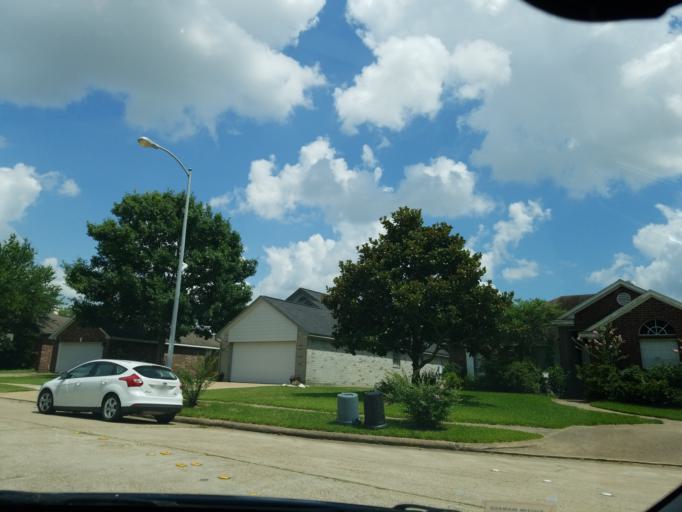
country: US
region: Texas
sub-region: Harris County
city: Cypress
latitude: 29.8712
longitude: -95.7343
